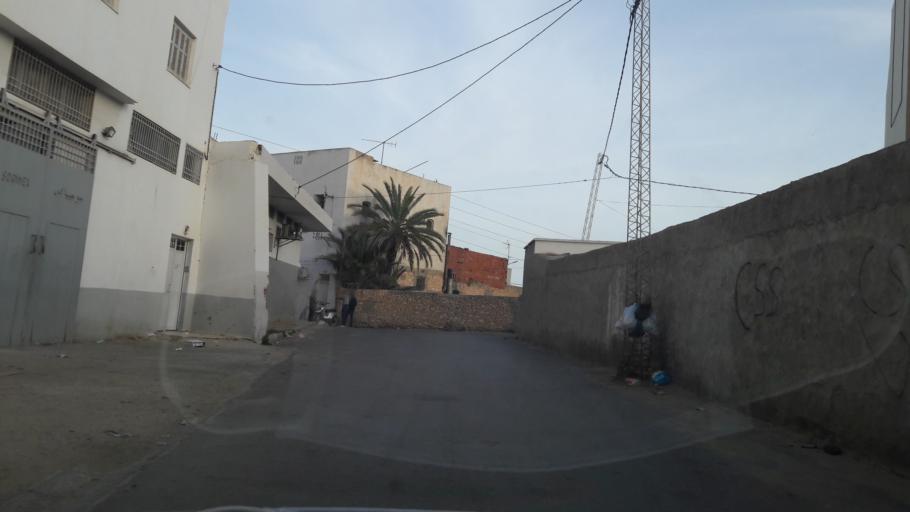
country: TN
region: Safaqis
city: Al Qarmadah
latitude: 34.8011
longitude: 10.7606
